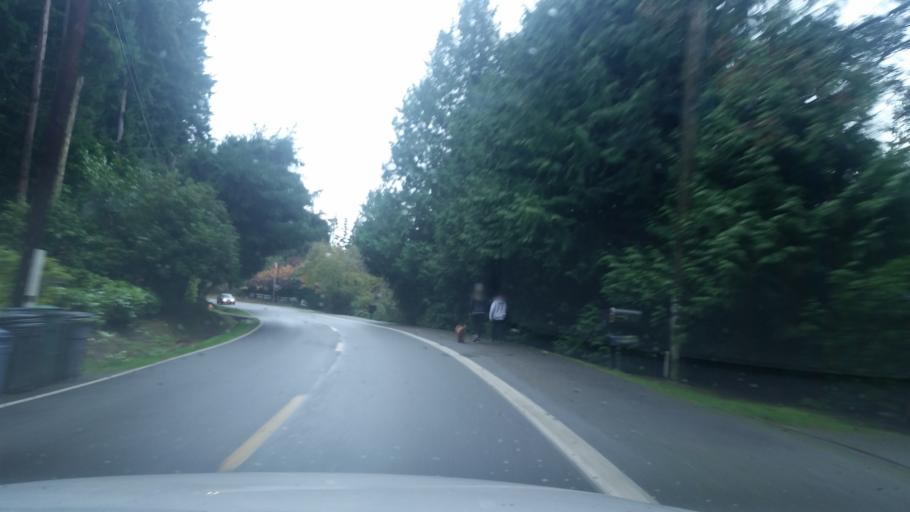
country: US
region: Washington
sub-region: Snohomish County
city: Woodway
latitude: 47.7956
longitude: -122.3835
